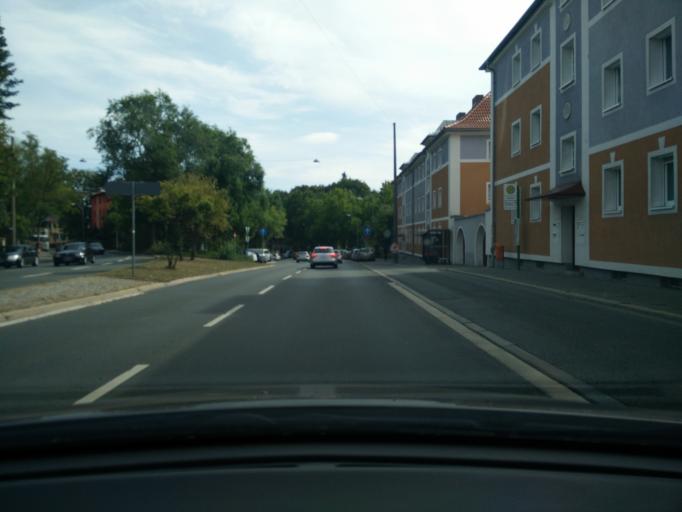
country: DE
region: Bavaria
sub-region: Regierungsbezirk Mittelfranken
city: Furth
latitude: 49.4812
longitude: 10.9710
